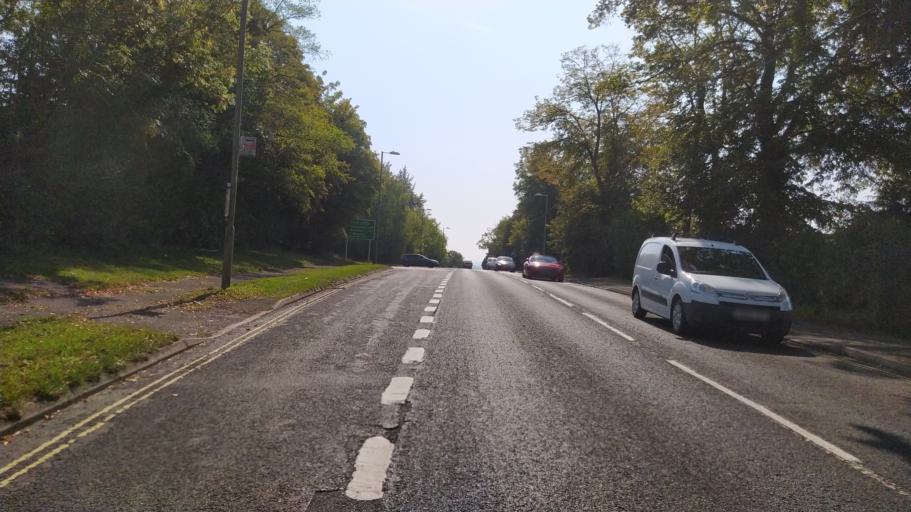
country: GB
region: England
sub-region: Hampshire
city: Andover
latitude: 51.1966
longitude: -1.4816
